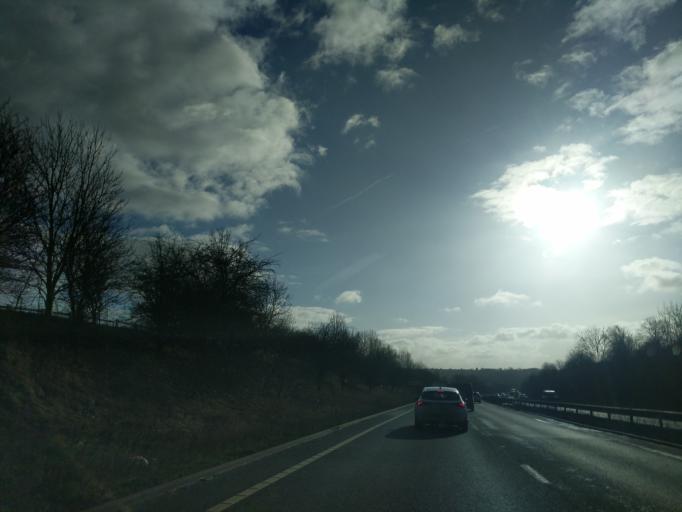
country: GB
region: England
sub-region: Derbyshire
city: Ripley
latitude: 53.0666
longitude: -1.4089
